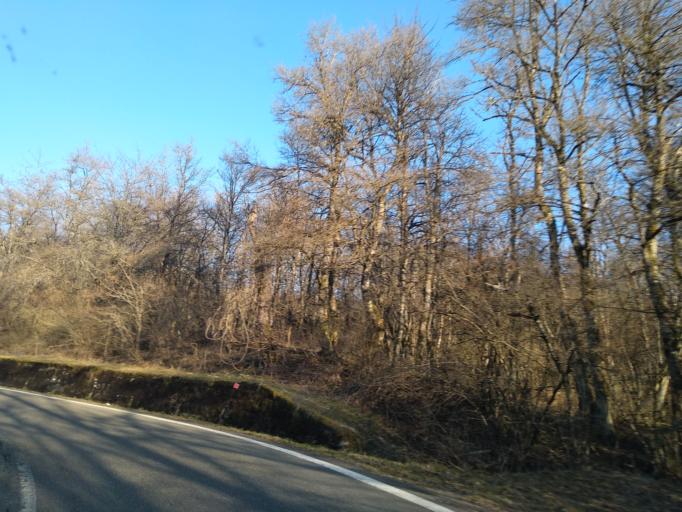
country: IT
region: Emilia-Romagna
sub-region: Provincia di Reggio Emilia
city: Busana
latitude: 44.4051
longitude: 10.3182
